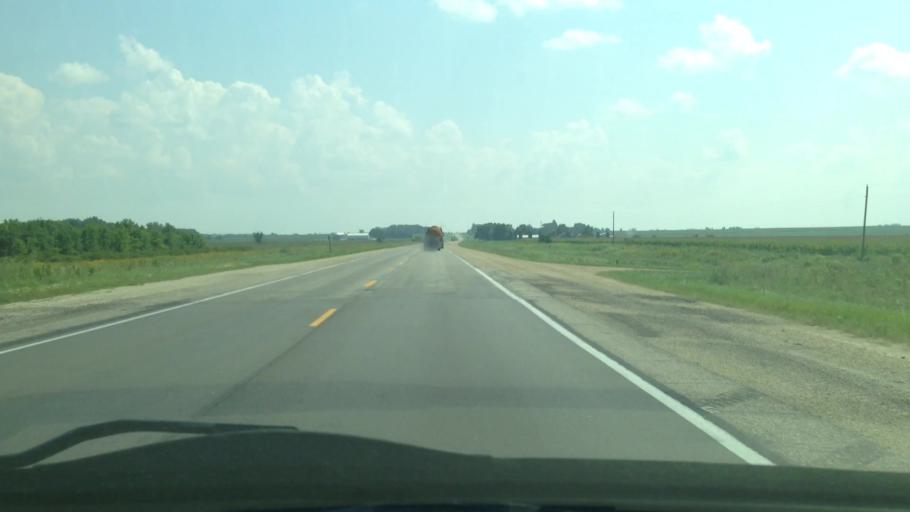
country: US
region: Iowa
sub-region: Chickasaw County
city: New Hampton
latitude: 43.2387
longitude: -92.2988
